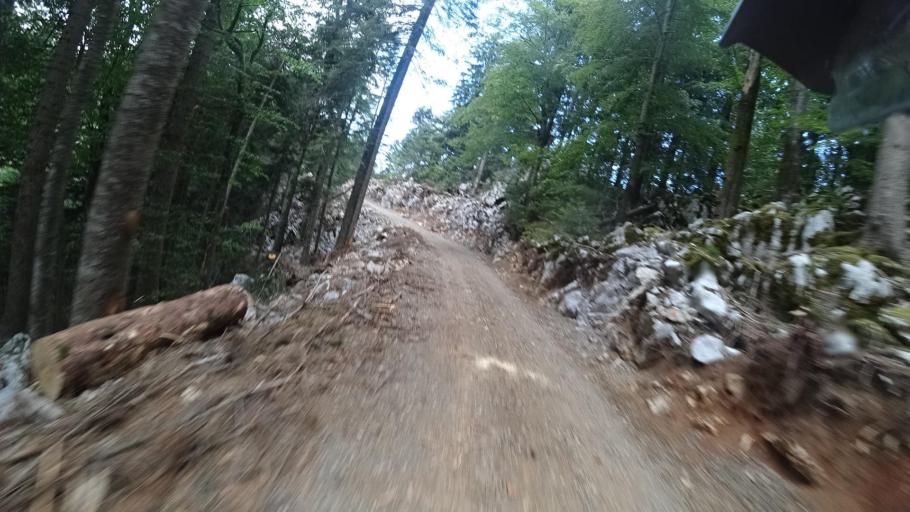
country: HR
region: Licko-Senjska
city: Senj
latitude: 45.1353
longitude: 14.9725
